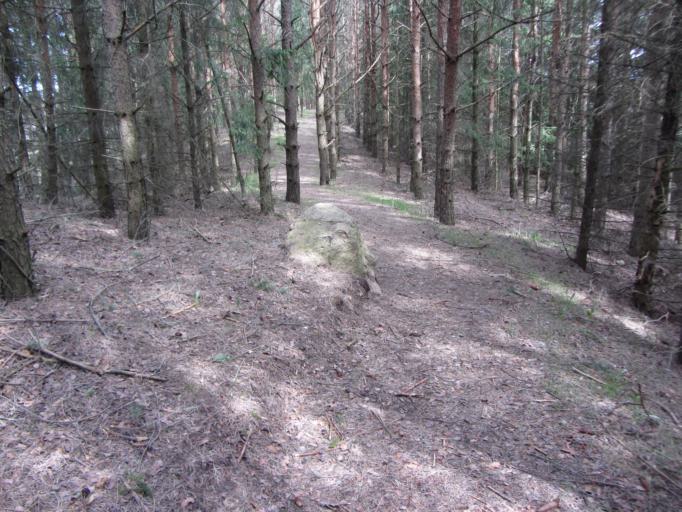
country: LT
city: Zarasai
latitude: 55.5831
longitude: 26.1482
